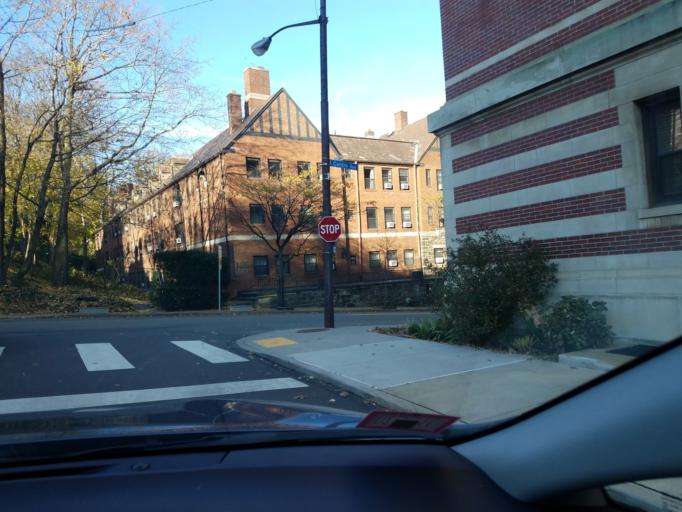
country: US
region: Pennsylvania
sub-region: Allegheny County
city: Bloomfield
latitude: 40.4512
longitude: -79.9540
